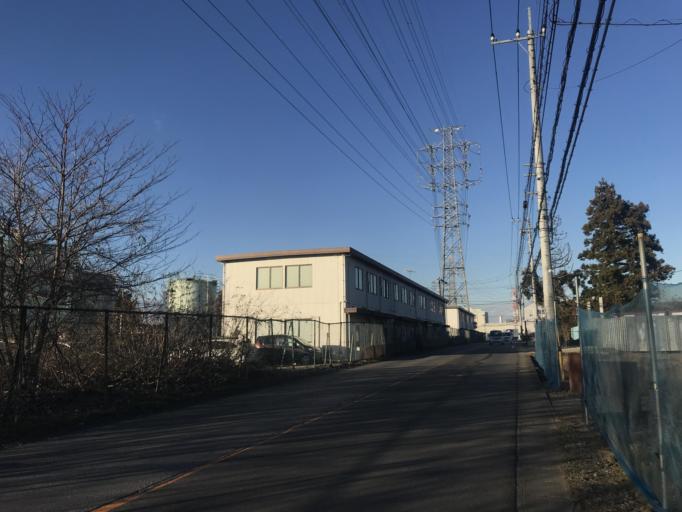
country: JP
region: Tochigi
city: Kaminokawa
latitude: 36.4467
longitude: 139.8714
